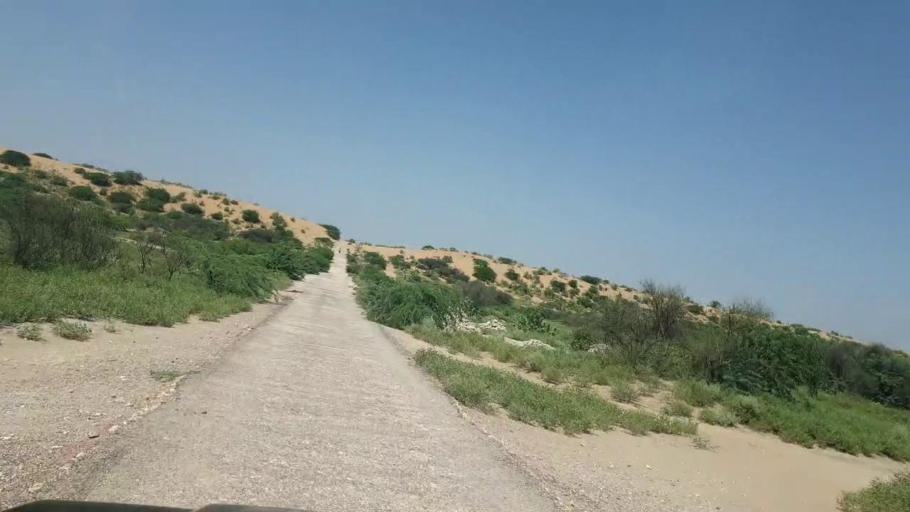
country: PK
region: Sindh
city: Chor
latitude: 25.3490
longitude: 70.3471
